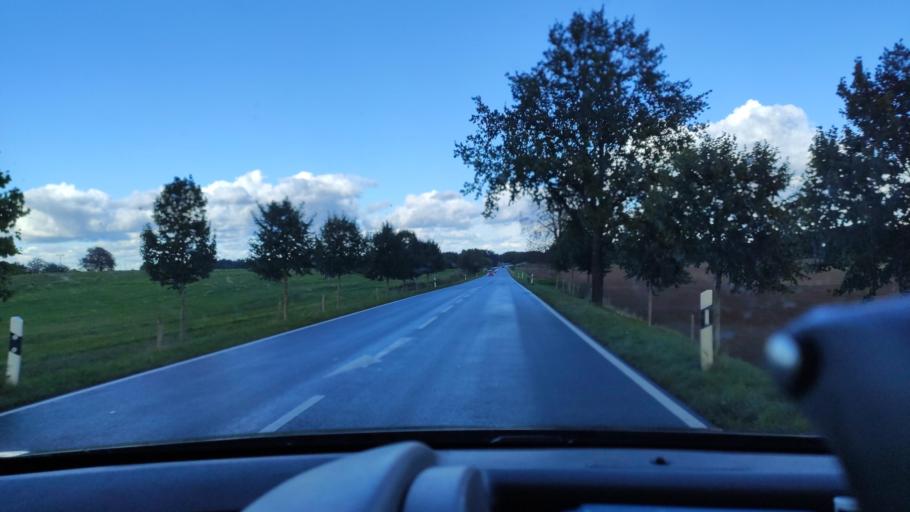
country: DE
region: Mecklenburg-Vorpommern
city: Tarnow
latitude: 53.7567
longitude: 12.0389
